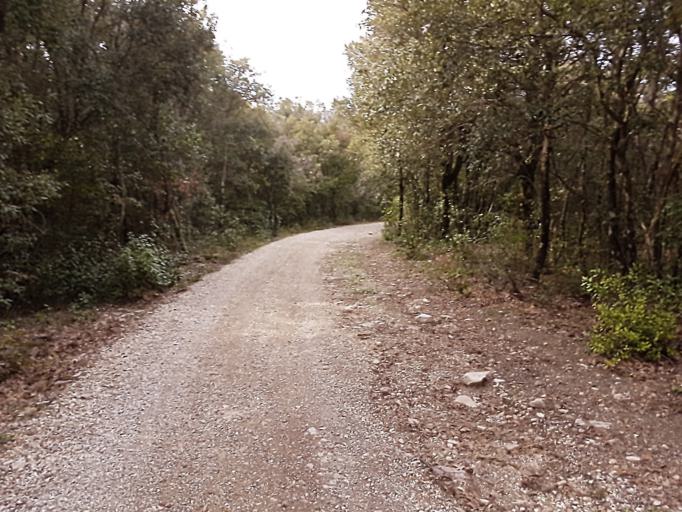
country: IT
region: Umbria
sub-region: Provincia di Perugia
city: Corciano
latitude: 43.1335
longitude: 12.3008
